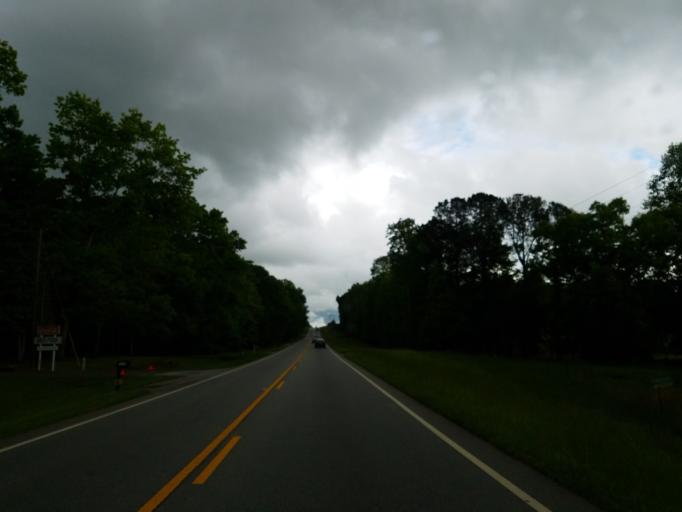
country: US
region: Georgia
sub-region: Lamar County
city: Barnesville
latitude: 33.0217
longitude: -84.1364
